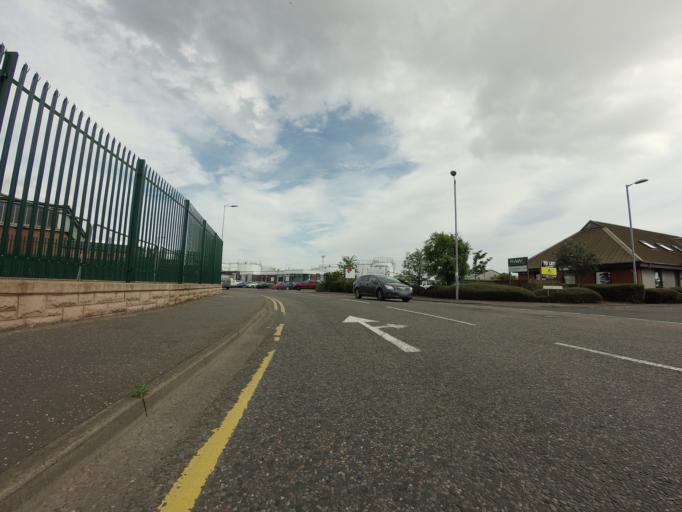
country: GB
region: Scotland
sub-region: Highland
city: Inverness
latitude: 57.4863
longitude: -4.2285
